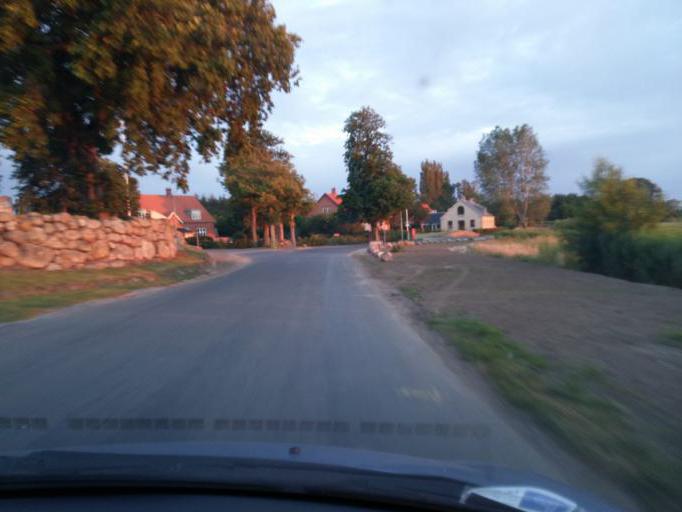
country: DK
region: South Denmark
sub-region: Kerteminde Kommune
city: Munkebo
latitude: 55.4256
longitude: 10.5827
